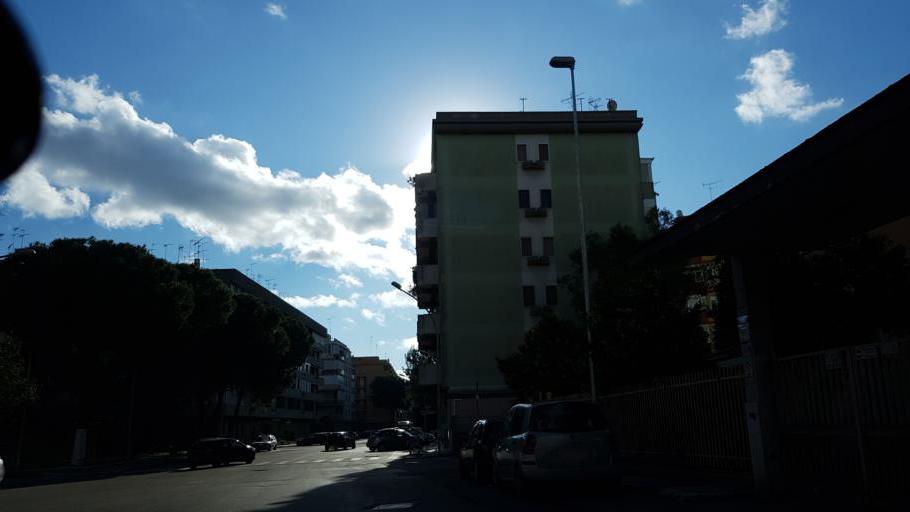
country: IT
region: Apulia
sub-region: Provincia di Brindisi
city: Brindisi
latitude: 40.6276
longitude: 17.9239
